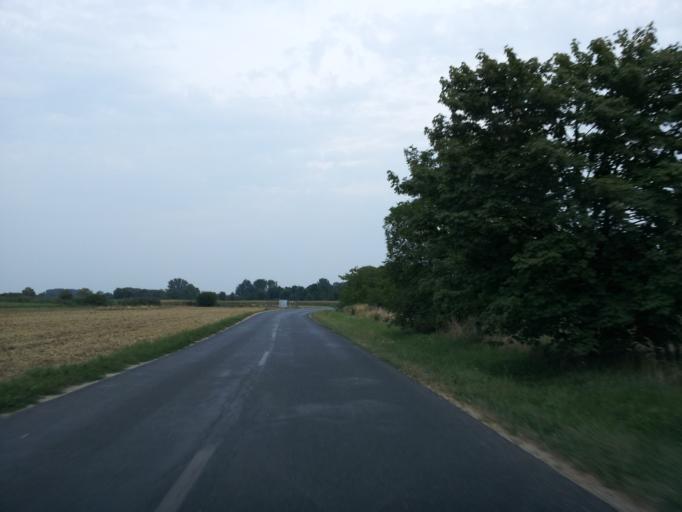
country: HU
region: Vas
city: Vep
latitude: 47.2057
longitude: 16.8130
